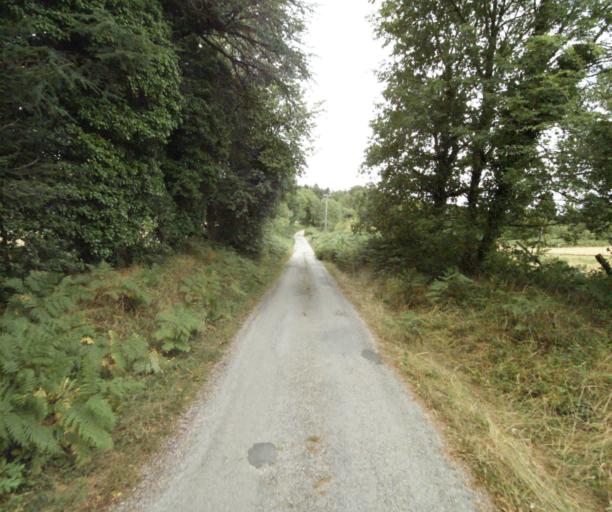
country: FR
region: Midi-Pyrenees
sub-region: Departement du Tarn
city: Soreze
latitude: 43.4250
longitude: 2.0943
